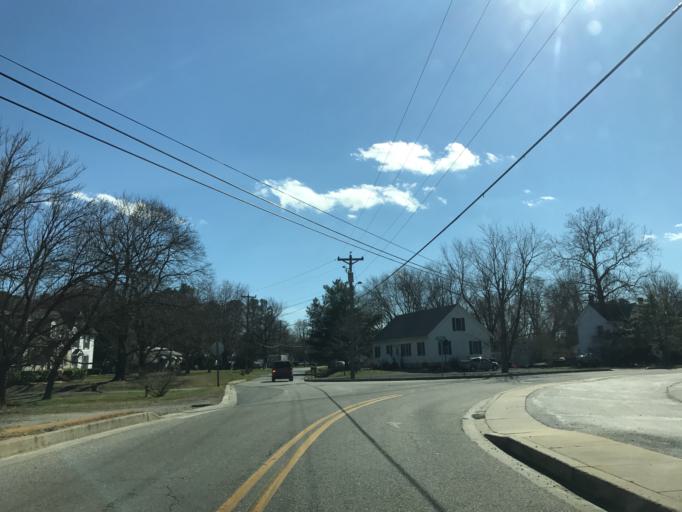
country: US
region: Maryland
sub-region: Kent County
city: Rock Hall
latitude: 39.1362
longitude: -76.2282
